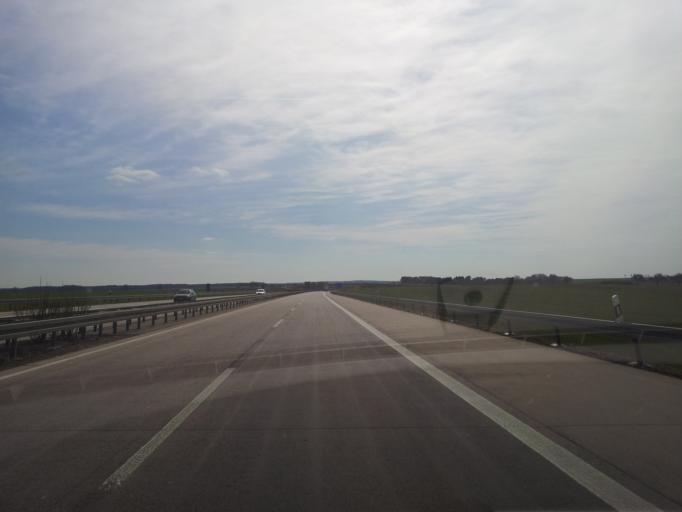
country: DE
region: Thuringia
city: Wolfershausen
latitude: 50.4450
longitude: 10.4424
